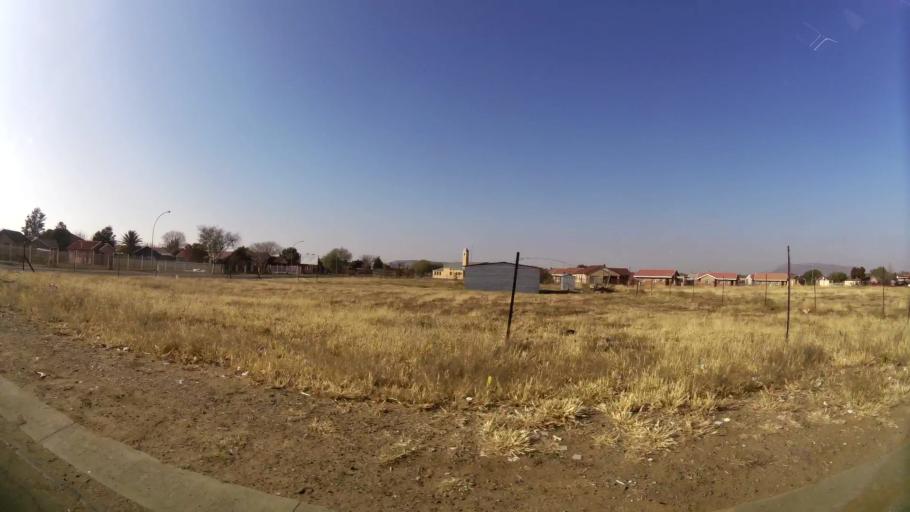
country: ZA
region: Orange Free State
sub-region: Mangaung Metropolitan Municipality
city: Bloemfontein
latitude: -29.1778
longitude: 26.1751
